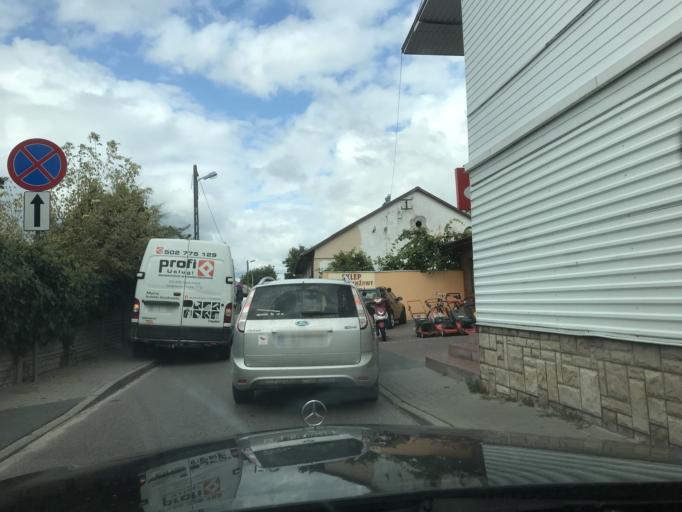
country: PL
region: Lublin Voivodeship
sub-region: Powiat janowski
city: Janow Lubelski
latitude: 50.7055
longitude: 22.4154
